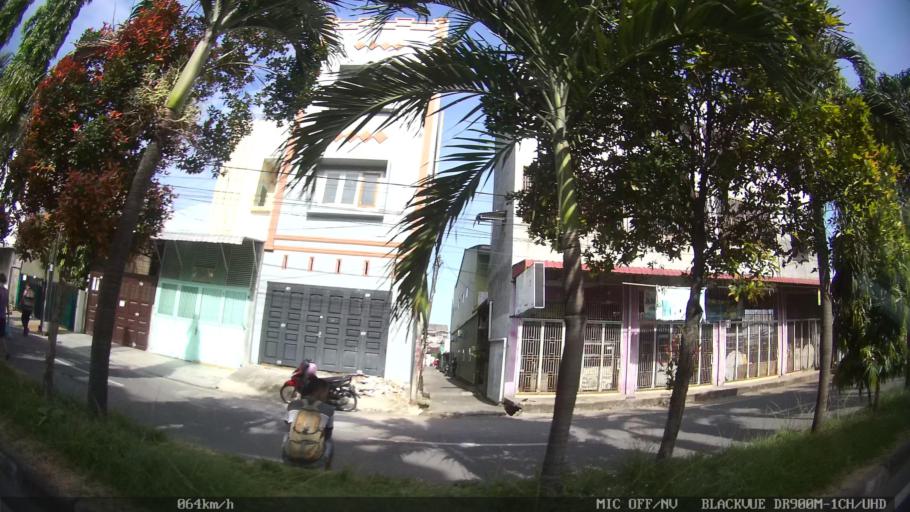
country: ID
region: North Sumatra
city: Medan
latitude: 3.5936
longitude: 98.6612
